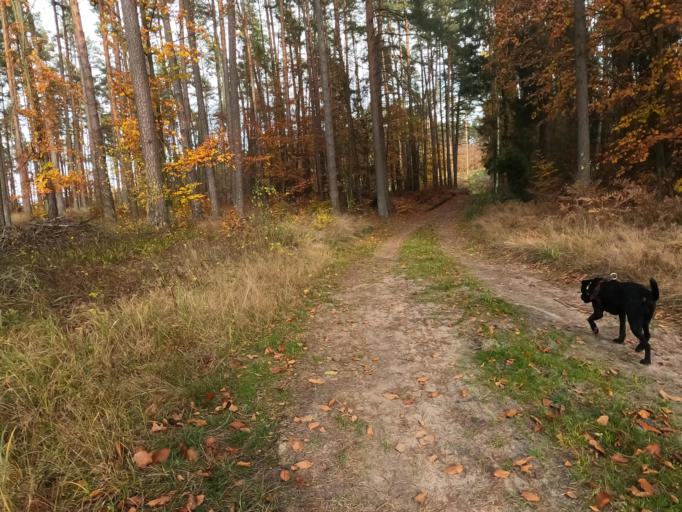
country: PL
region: Pomeranian Voivodeship
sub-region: Powiat starogardzki
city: Skarszewy
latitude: 54.0092
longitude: 18.4633
